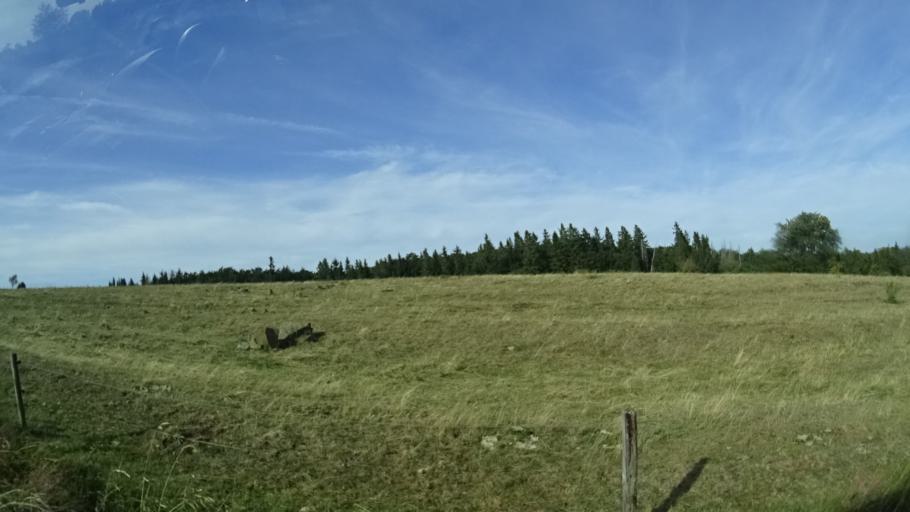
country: DE
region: Bavaria
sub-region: Regierungsbezirk Unterfranken
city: Hausen
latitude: 50.4994
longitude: 10.0845
